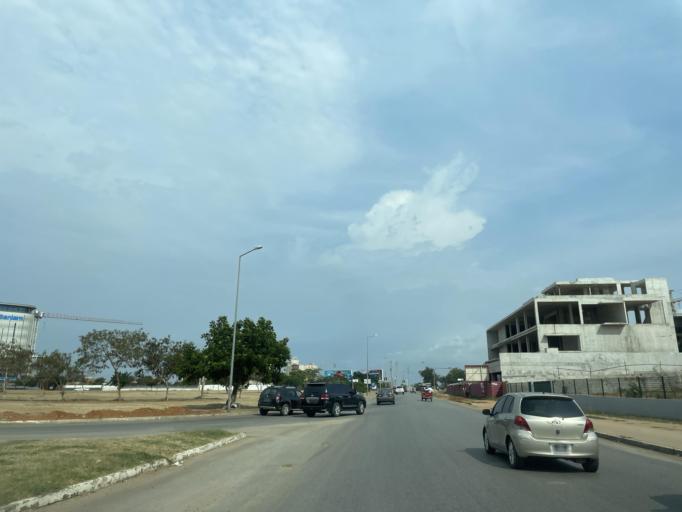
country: AO
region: Luanda
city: Luanda
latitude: -8.9208
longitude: 13.1900
